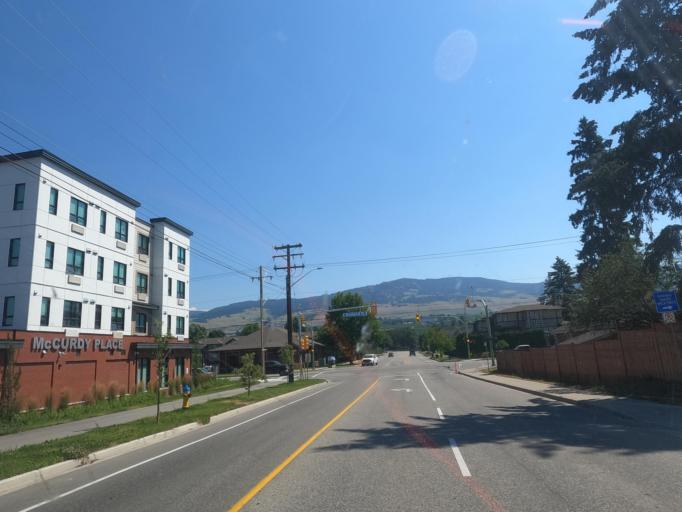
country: CA
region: British Columbia
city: Kelowna
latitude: 49.9011
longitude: -119.3876
